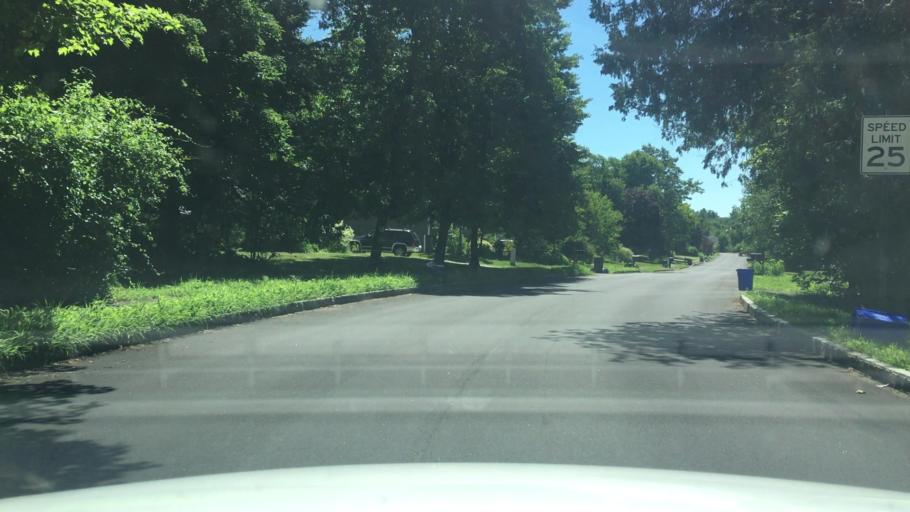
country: US
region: New Hampshire
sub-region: Merrimack County
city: Boscawen
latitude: 43.2754
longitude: -71.6034
